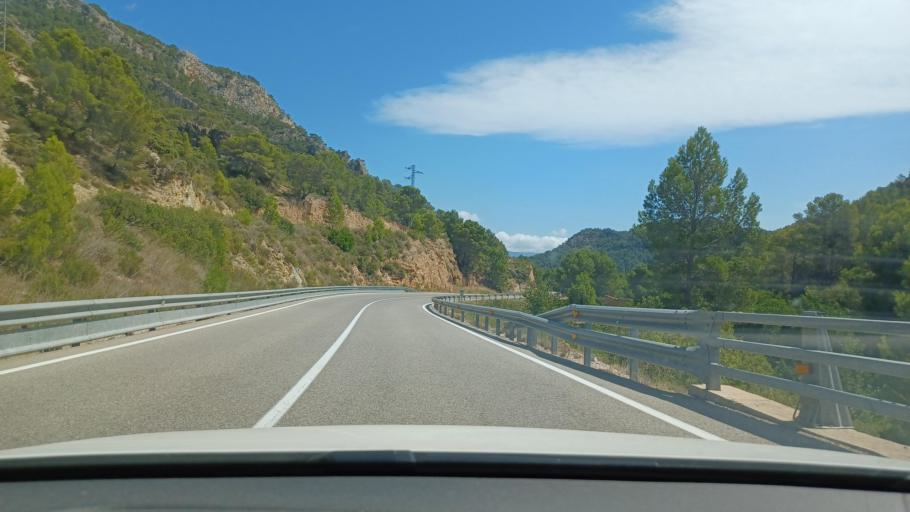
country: ES
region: Catalonia
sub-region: Provincia de Tarragona
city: Bot
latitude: 40.9771
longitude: 0.4196
